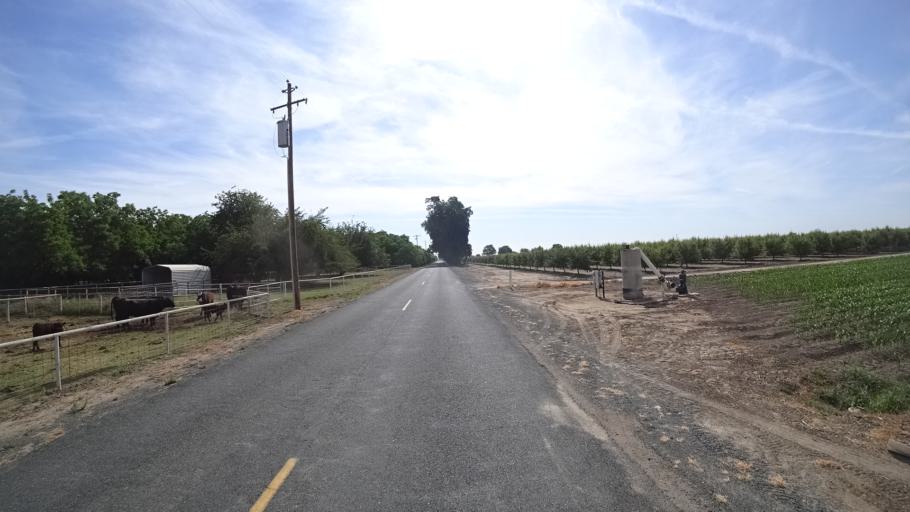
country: US
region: California
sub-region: Kings County
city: Lucerne
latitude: 36.4158
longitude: -119.6517
